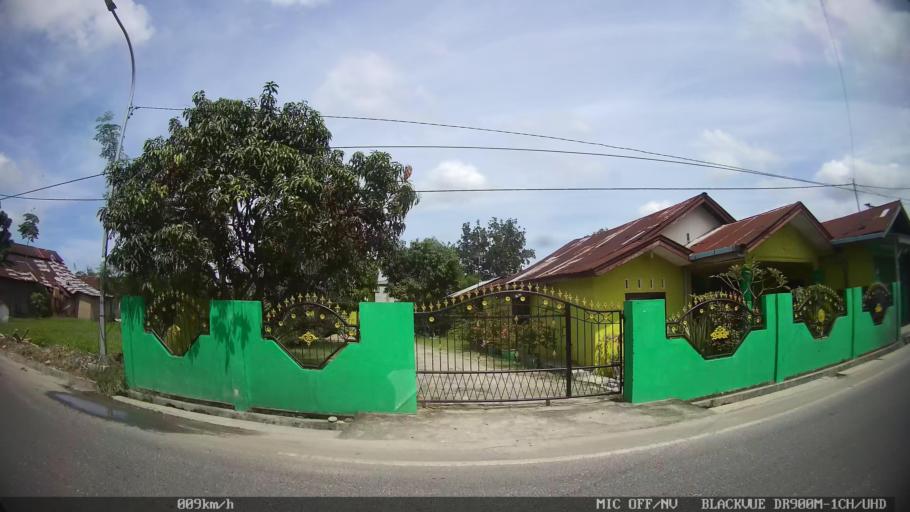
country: ID
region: North Sumatra
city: Percut
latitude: 3.5951
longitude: 98.8598
